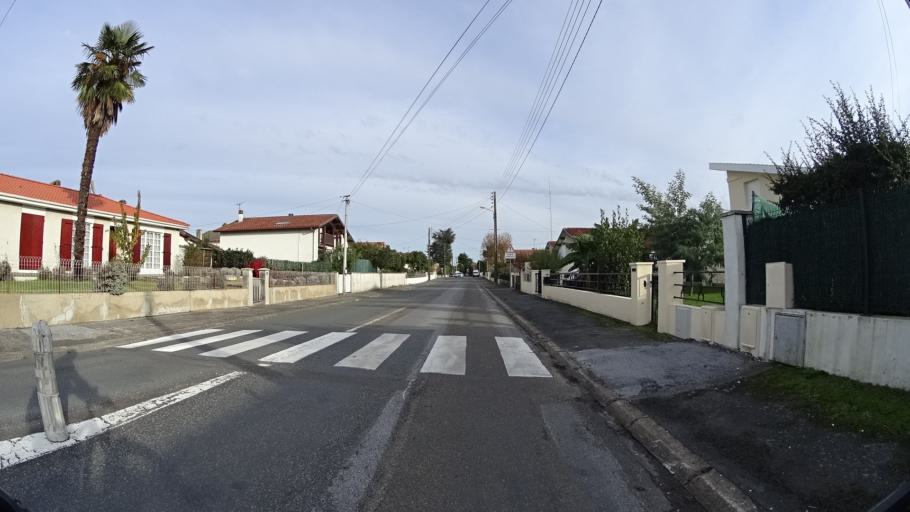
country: FR
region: Aquitaine
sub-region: Departement des Landes
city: Saint-Paul-les-Dax
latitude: 43.7296
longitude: -1.0551
